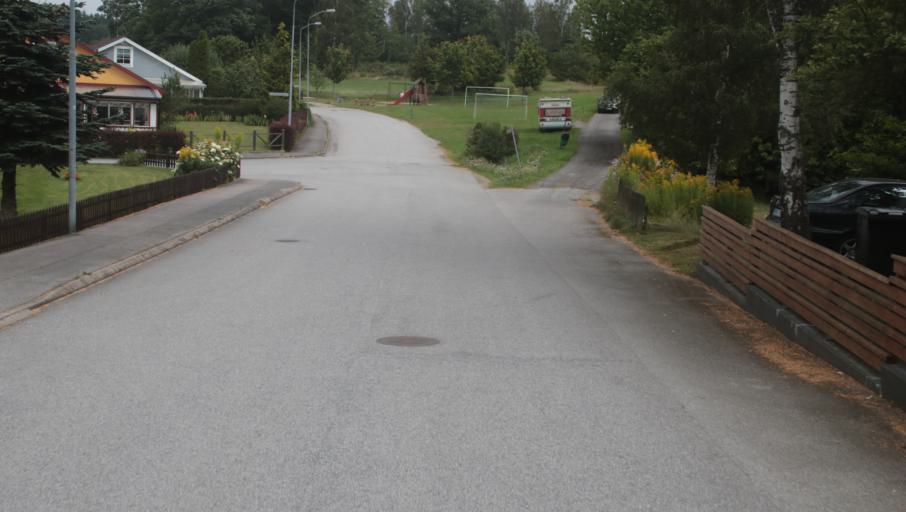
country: SE
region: Blekinge
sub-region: Karlshamns Kommun
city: Karlshamn
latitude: 56.2143
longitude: 14.9518
